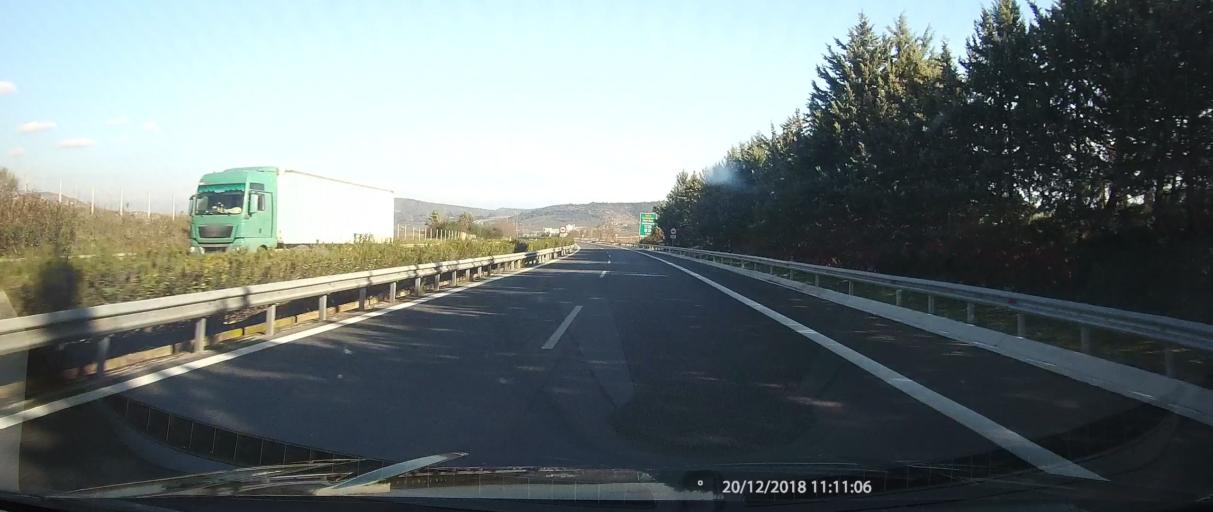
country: GR
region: Peloponnese
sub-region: Nomos Korinthias
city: Ayios Vasilios
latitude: 37.8278
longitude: 22.8018
